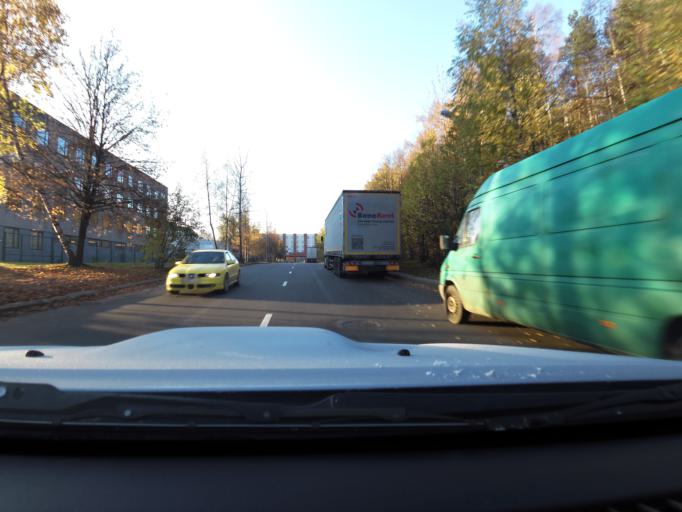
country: LT
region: Vilnius County
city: Vilkpede
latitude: 54.6328
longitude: 25.2562
